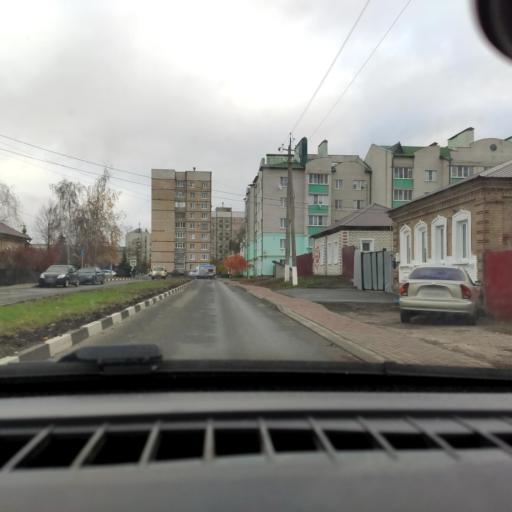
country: RU
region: Belgorod
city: Alekseyevka
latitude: 50.6281
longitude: 38.6955
